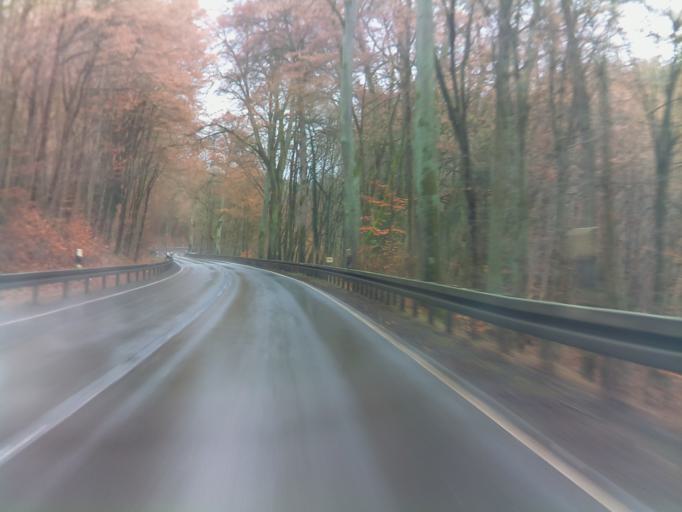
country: DE
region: Hesse
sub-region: Regierungsbezirk Giessen
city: Schlitz
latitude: 50.6783
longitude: 9.5088
